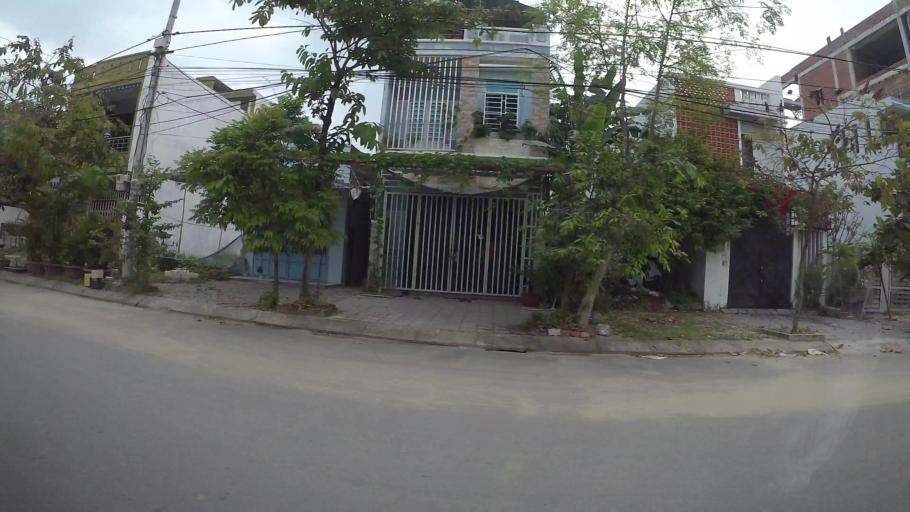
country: VN
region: Da Nang
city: Son Tra
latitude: 16.0826
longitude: 108.2413
